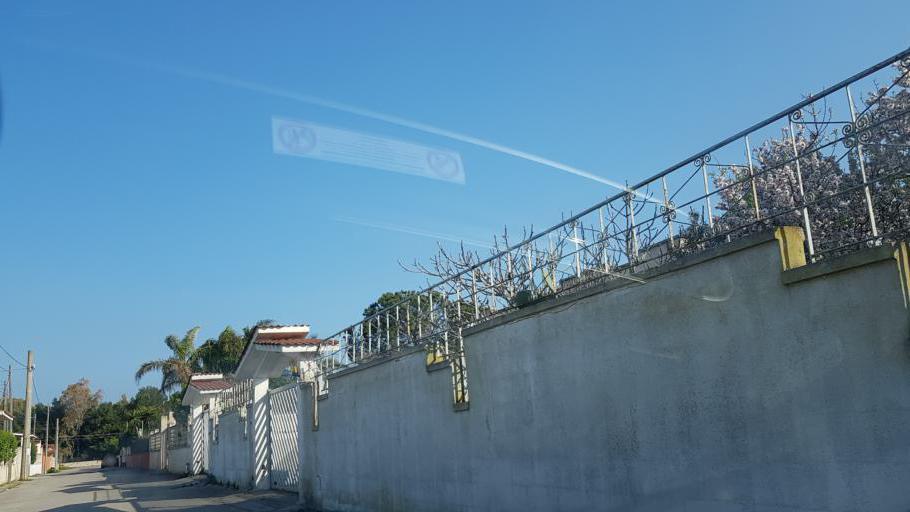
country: IT
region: Apulia
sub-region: Provincia di Brindisi
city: Materdomini
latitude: 40.6677
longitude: 17.9426
